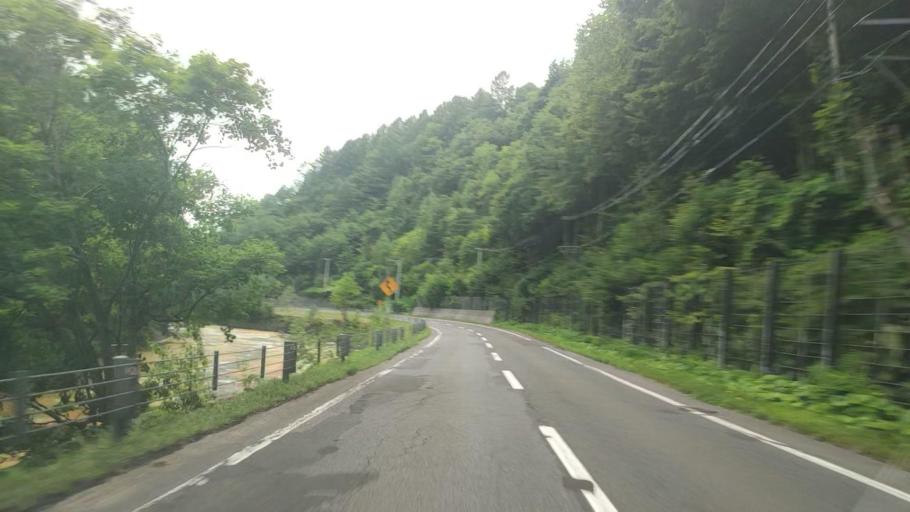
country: JP
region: Hokkaido
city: Date
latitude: 42.6285
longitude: 141.0263
